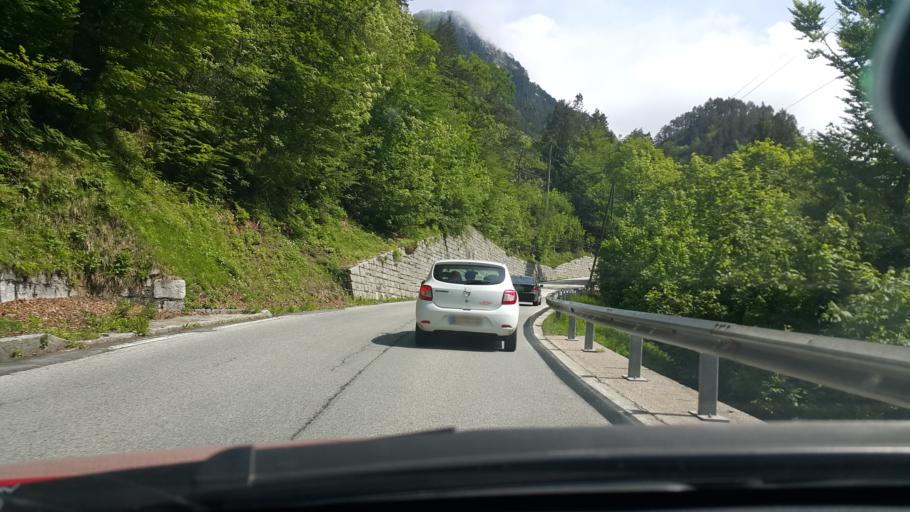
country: AT
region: Carinthia
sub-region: Politischer Bezirk Klagenfurt Land
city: Ferlach
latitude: 46.4835
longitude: 14.2618
